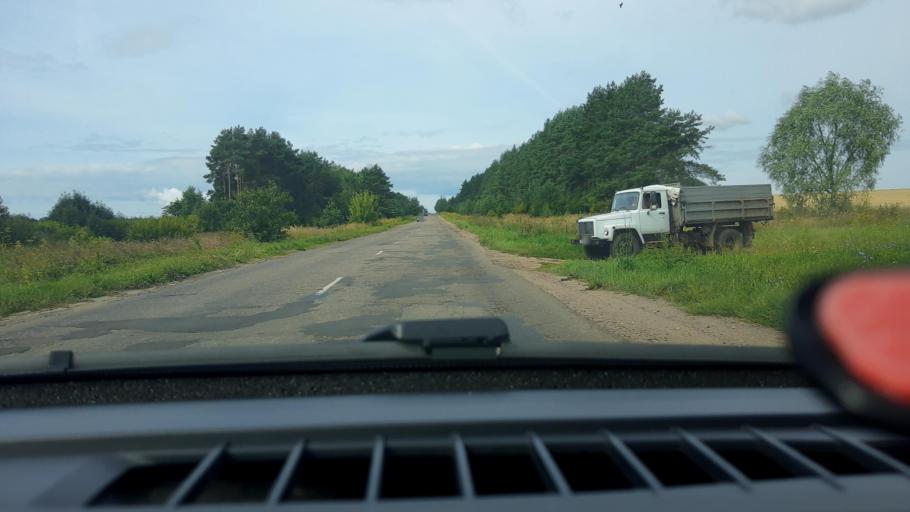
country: RU
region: Nizjnij Novgorod
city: Bogorodsk
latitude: 56.0657
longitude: 43.6237
